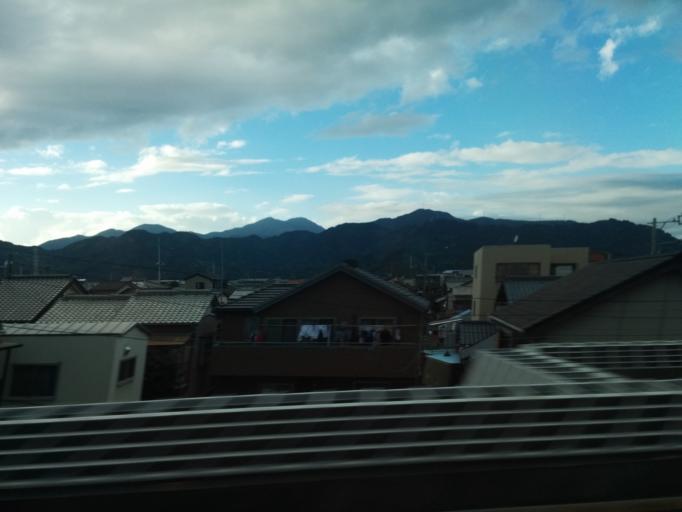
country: JP
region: Shizuoka
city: Shizuoka-shi
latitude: 35.0262
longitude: 138.4727
